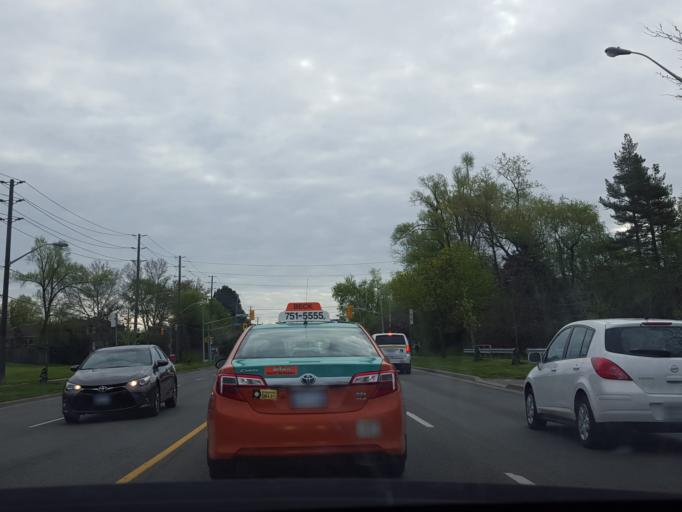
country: CA
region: Ontario
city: Willowdale
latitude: 43.7888
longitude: -79.3749
